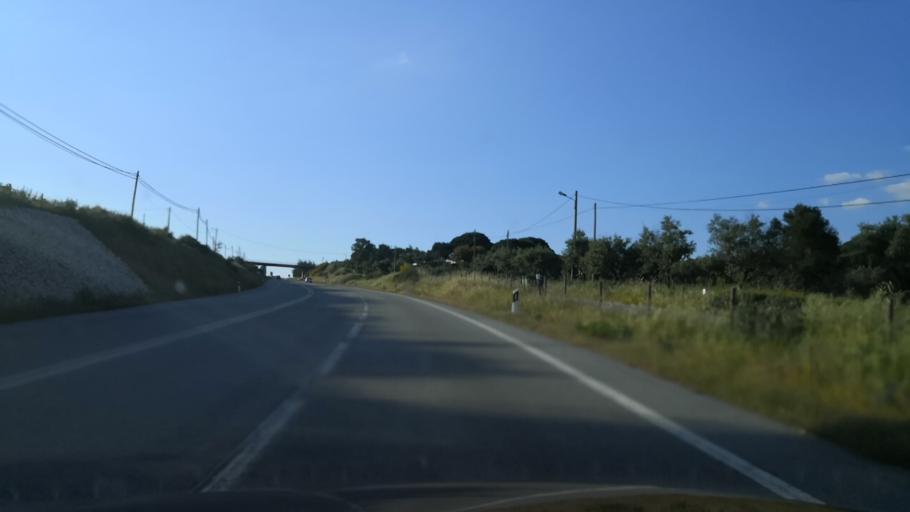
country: PT
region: Portalegre
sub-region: Portalegre
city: Portalegre
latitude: 39.3026
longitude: -7.4394
